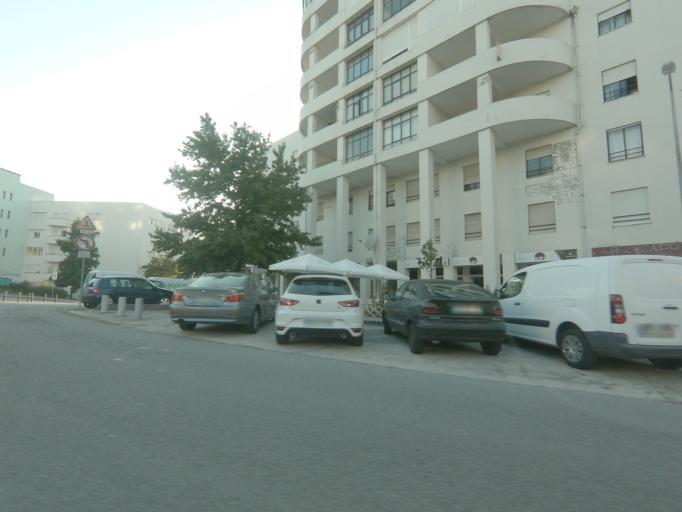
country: PT
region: Vila Real
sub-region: Vila Real
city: Vila Real
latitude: 41.3046
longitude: -7.7445
